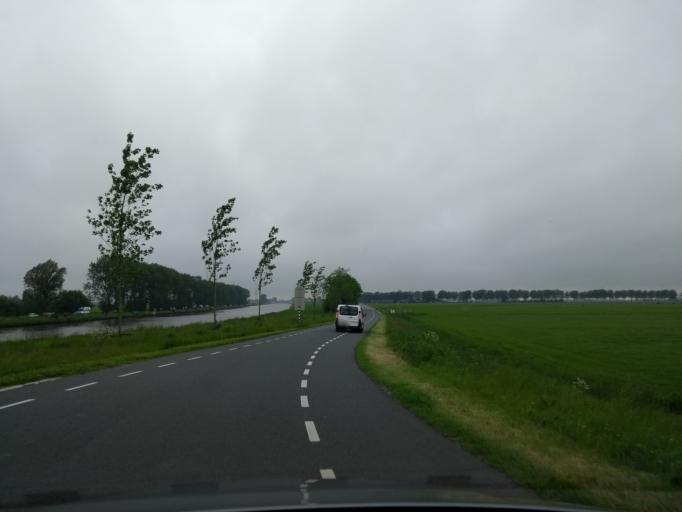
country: NL
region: Groningen
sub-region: Gemeente Zuidhorn
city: Aduard
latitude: 53.2593
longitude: 6.5013
